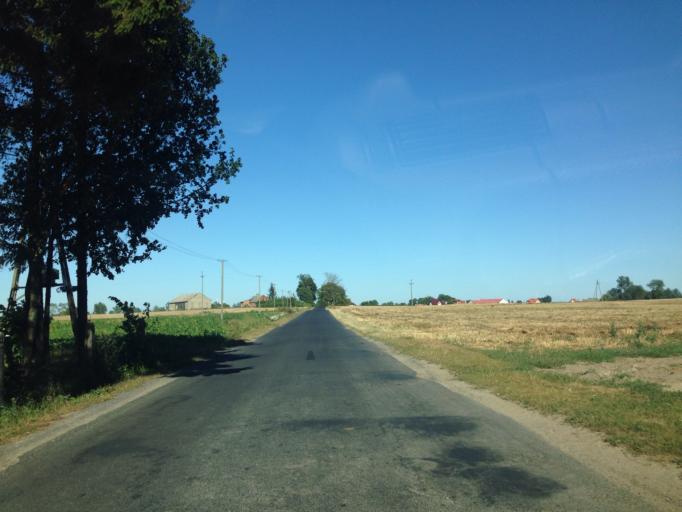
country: PL
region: Kujawsko-Pomorskie
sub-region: Powiat brodnicki
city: Brodnica
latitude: 53.2084
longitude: 19.4295
